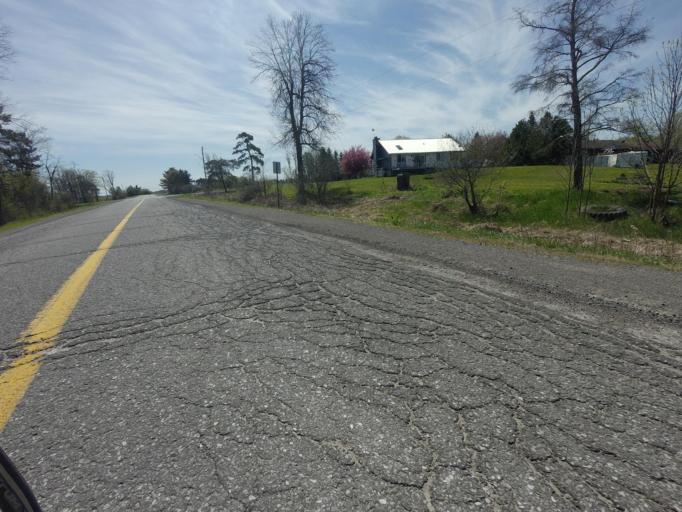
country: CA
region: Ontario
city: Carleton Place
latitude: 45.3662
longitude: -76.1083
